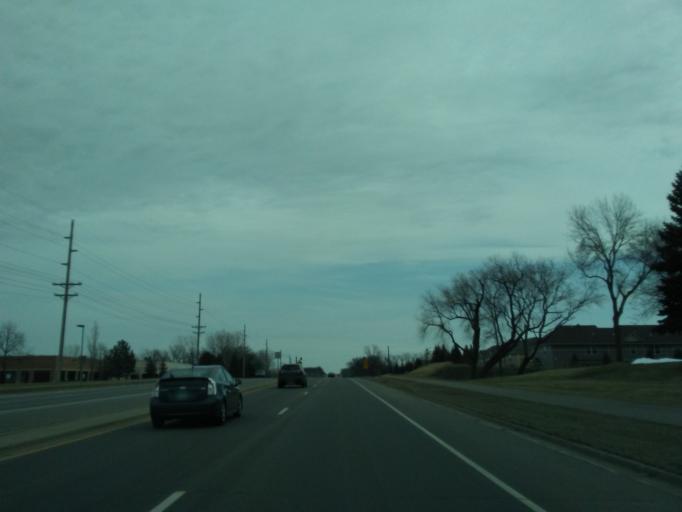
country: US
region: Minnesota
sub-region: Dakota County
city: Eagan
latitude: 44.8335
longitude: -93.1430
